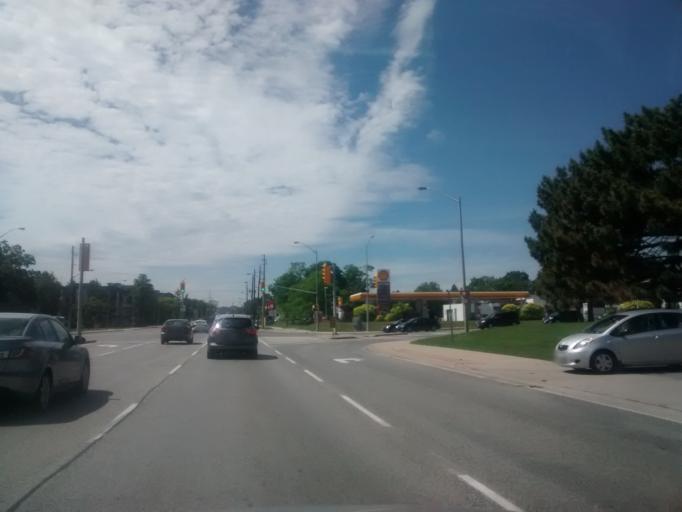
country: CA
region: Ontario
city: Burlington
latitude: 43.3565
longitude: -79.8102
